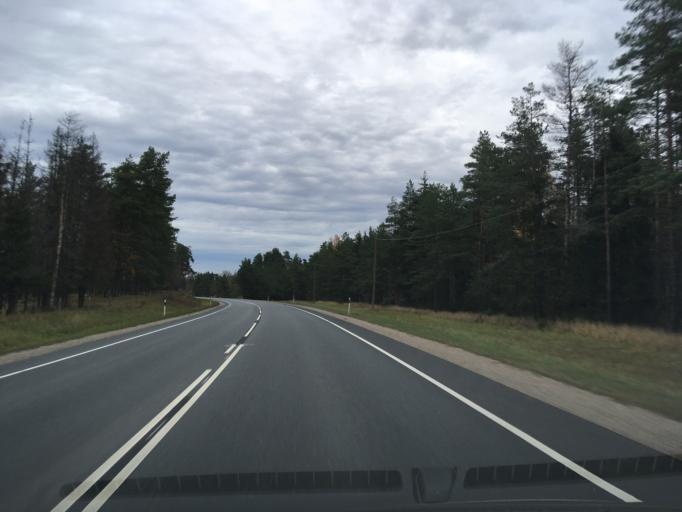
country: EE
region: Harju
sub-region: Nissi vald
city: Turba
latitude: 59.0219
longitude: 24.1471
